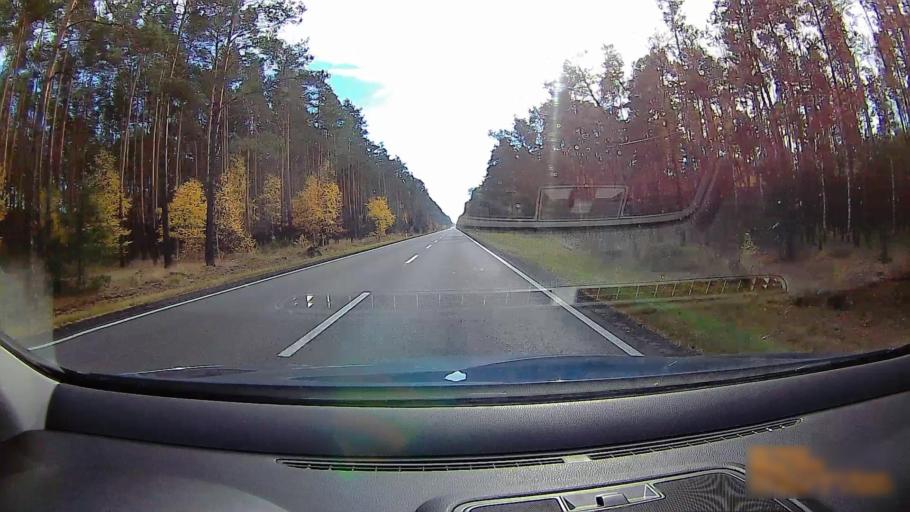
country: PL
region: Greater Poland Voivodeship
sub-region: Powiat ostrzeszowski
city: Ostrzeszow
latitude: 51.4737
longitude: 17.8905
